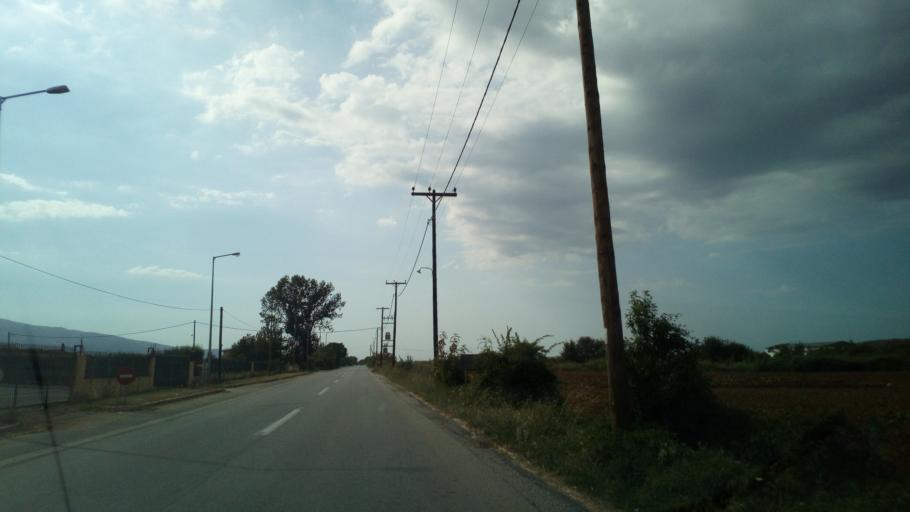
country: GR
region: Central Macedonia
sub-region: Nomos Thessalonikis
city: Gerakarou
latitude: 40.5779
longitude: 23.2733
